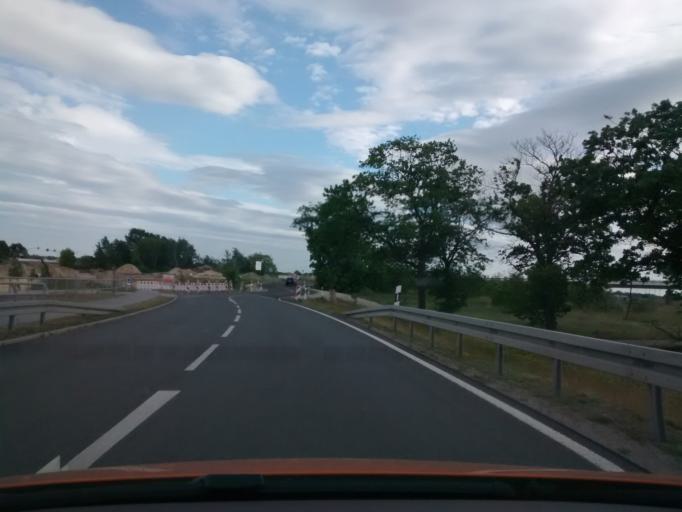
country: DE
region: Berlin
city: Bohnsdorf
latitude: 52.3710
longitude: 13.5496
